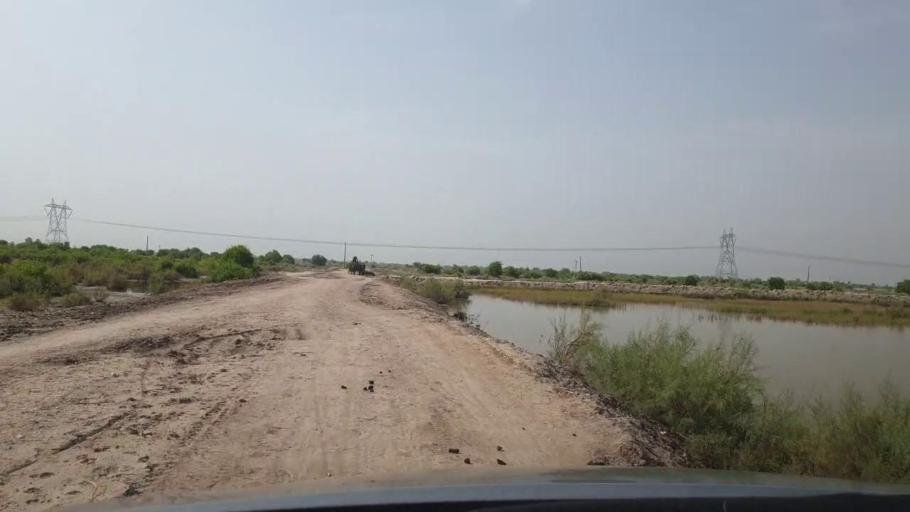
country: PK
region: Sindh
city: Rohri
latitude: 27.6776
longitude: 69.0118
